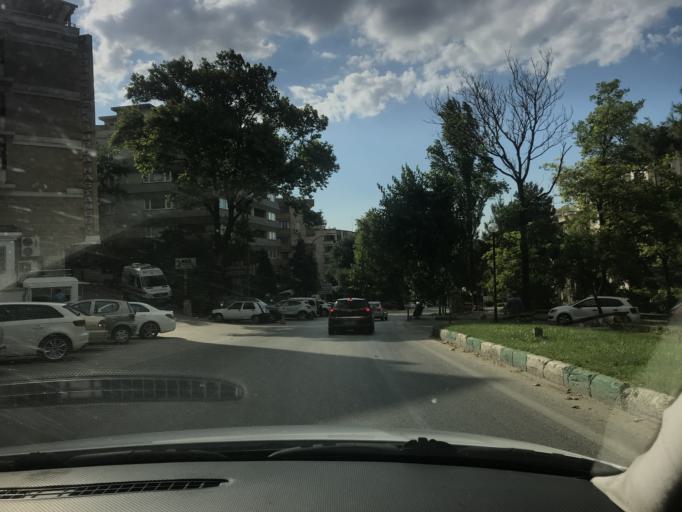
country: TR
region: Bursa
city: Yildirim
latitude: 40.2042
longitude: 29.0209
